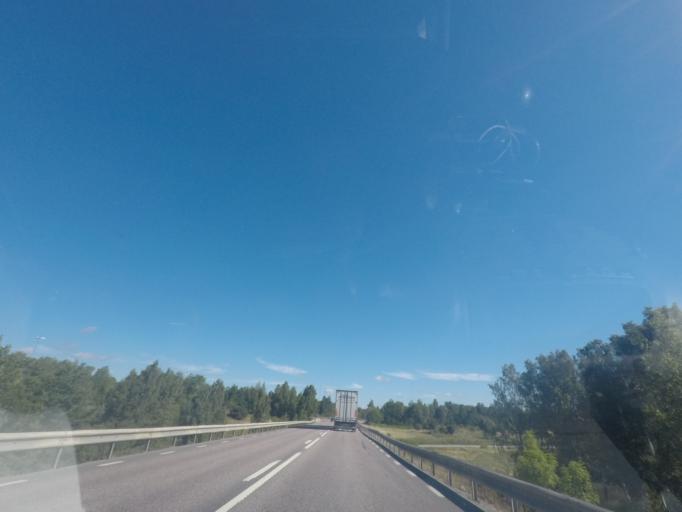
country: SE
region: Soedermanland
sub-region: Strangnas Kommun
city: Strangnas
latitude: 59.3858
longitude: 16.9879
